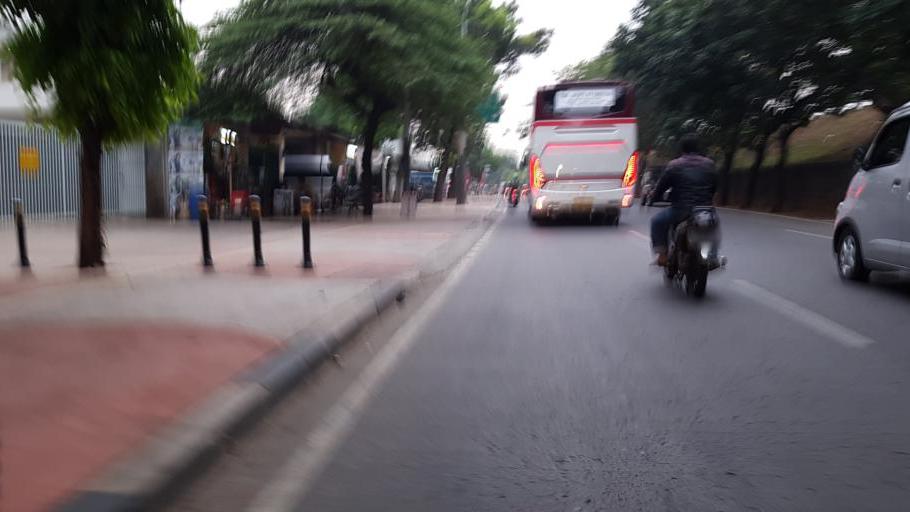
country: ID
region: Jakarta Raya
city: Jakarta
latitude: -6.3065
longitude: 106.8908
